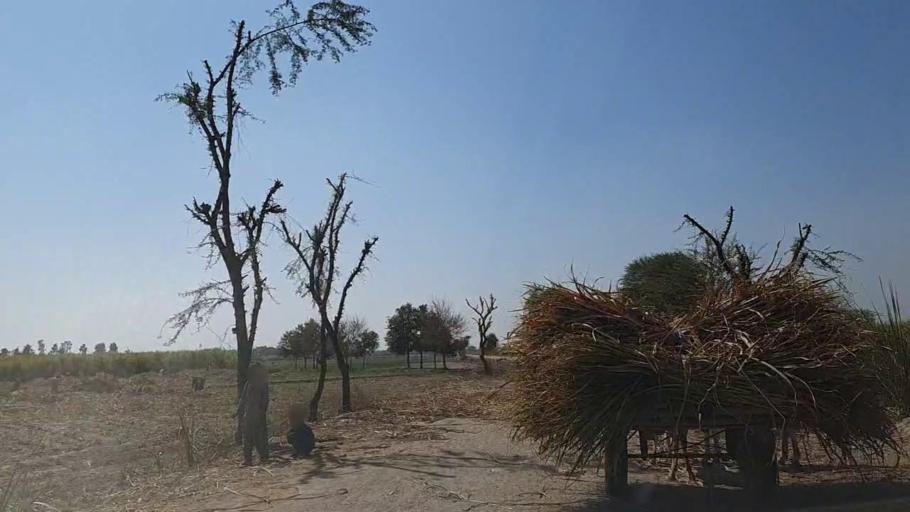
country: PK
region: Sindh
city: Samaro
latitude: 25.3705
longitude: 69.3260
